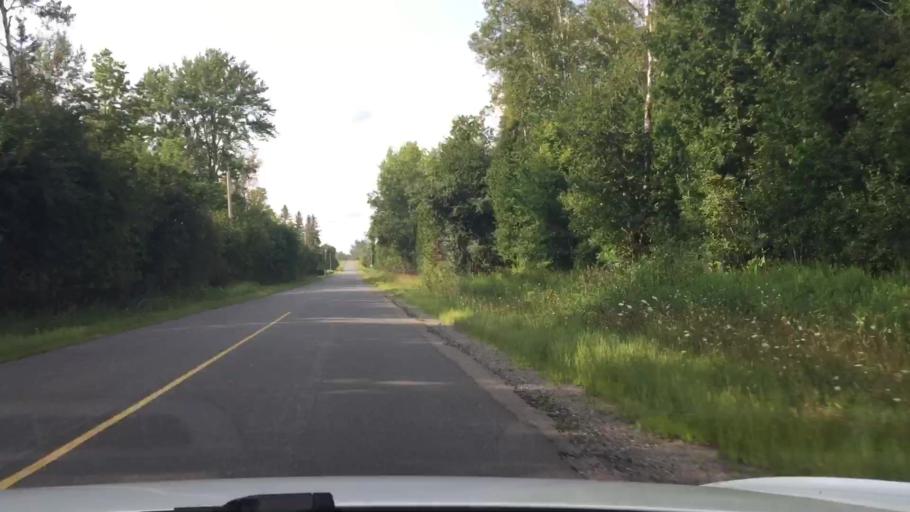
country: CA
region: Ontario
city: Oshawa
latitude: 43.9477
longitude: -78.7511
